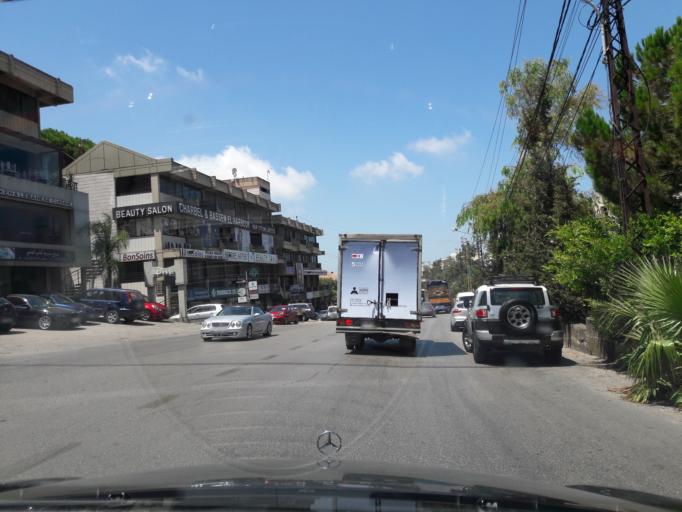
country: LB
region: Mont-Liban
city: Djounie
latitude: 33.9211
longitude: 35.6338
